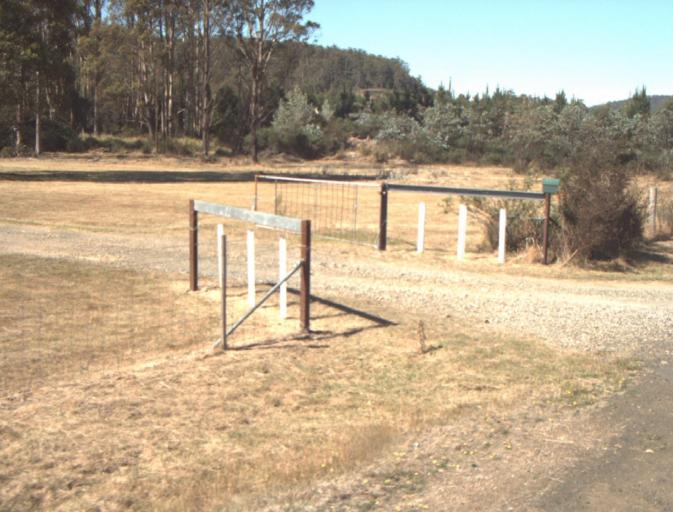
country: AU
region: Tasmania
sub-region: Launceston
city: Newstead
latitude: -41.3289
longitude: 147.3108
